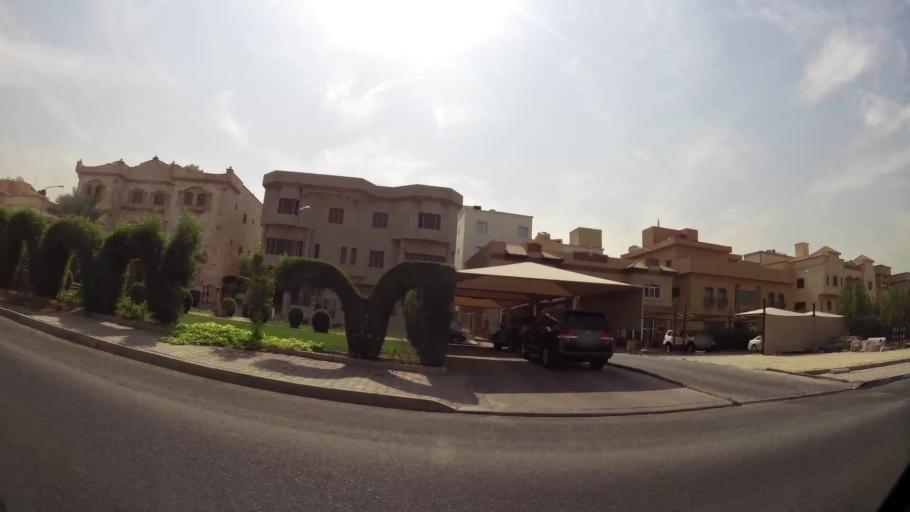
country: KW
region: Al Farwaniyah
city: Janub as Surrah
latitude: 29.2889
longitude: 48.0114
